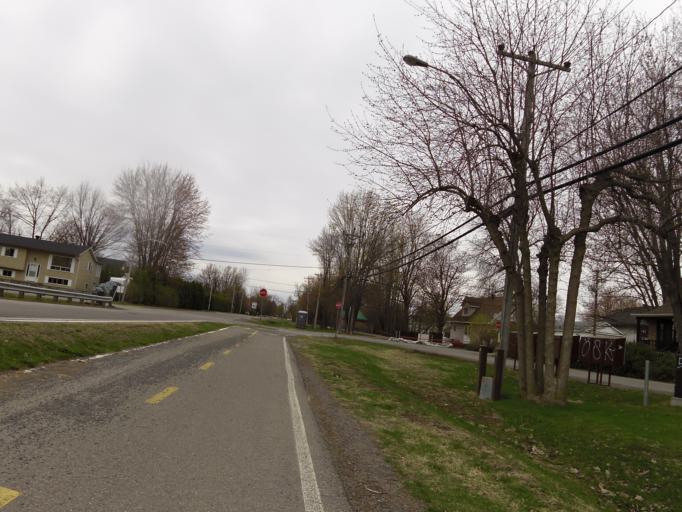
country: CA
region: Quebec
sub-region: Laurentides
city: Sainte-Marthe-sur-le-Lac
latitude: 45.5211
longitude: -73.9474
